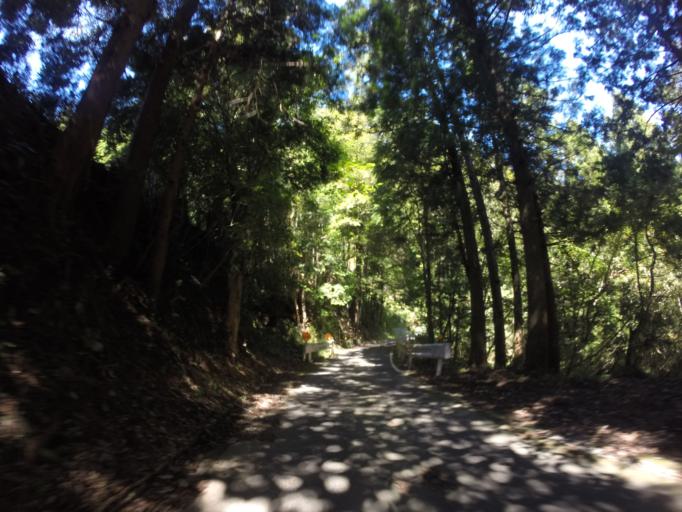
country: JP
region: Shizuoka
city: Fujieda
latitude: 34.9537
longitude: 138.1665
